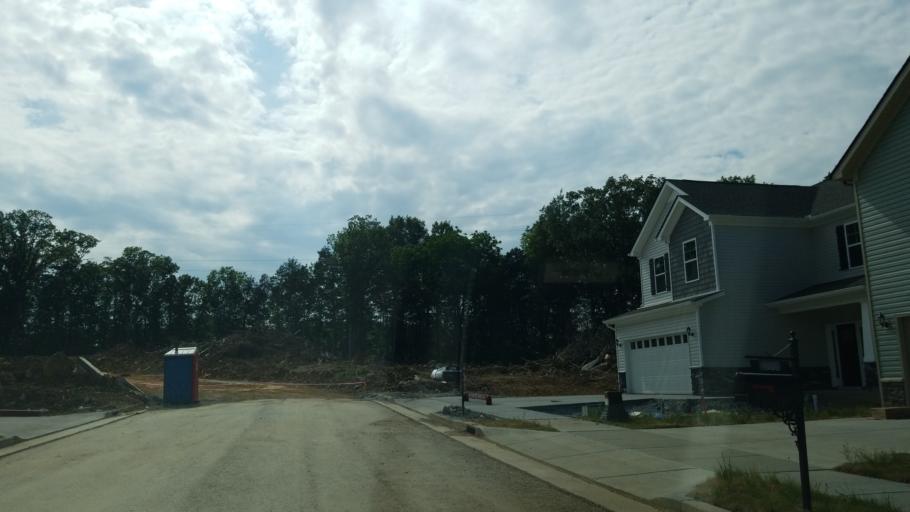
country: US
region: Tennessee
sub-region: Rutherford County
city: La Vergne
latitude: 36.0558
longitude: -86.5957
